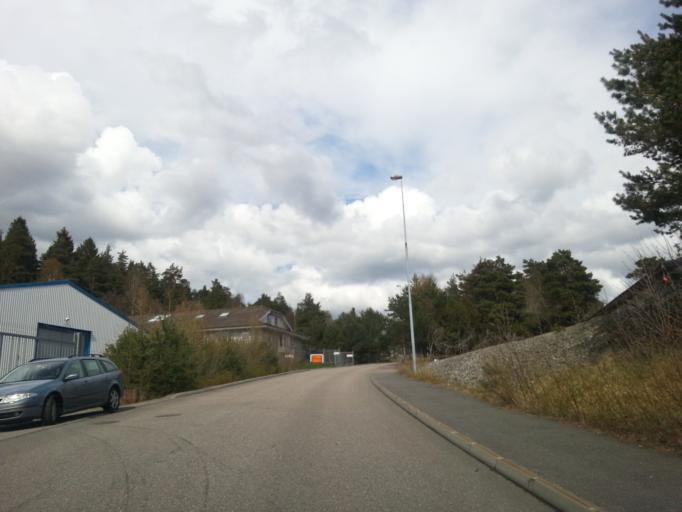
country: SE
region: Vaestra Goetaland
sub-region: Kungalvs Kommun
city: Kungalv
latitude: 57.8799
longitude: 11.9301
